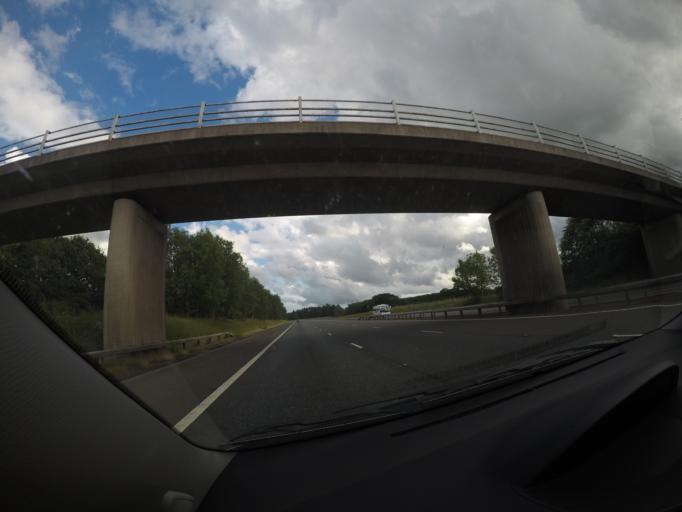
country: GB
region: Scotland
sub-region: Dumfries and Galloway
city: Lochmaben
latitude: 55.1825
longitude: -3.4055
